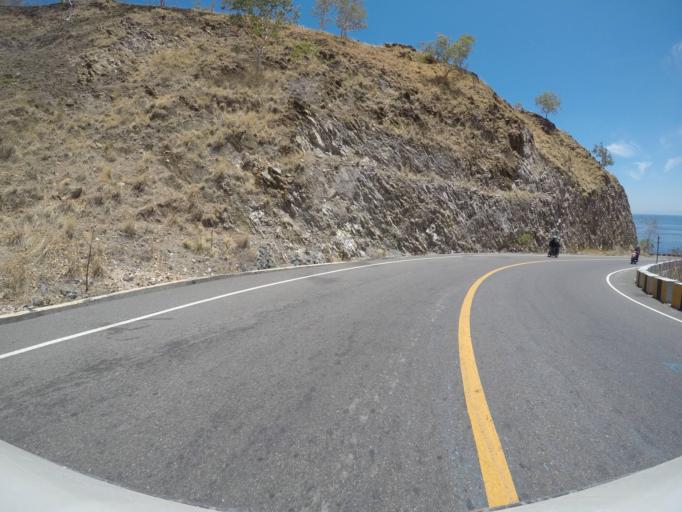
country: TL
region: Manatuto
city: Manatuto
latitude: -8.4786
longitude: 125.9407
